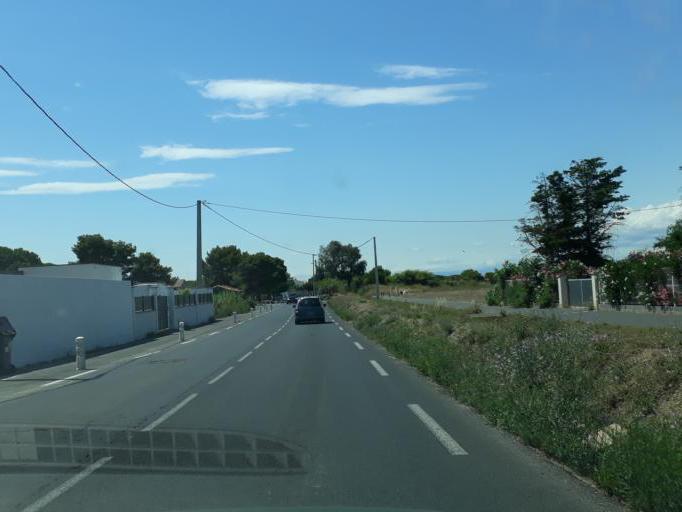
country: FR
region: Languedoc-Roussillon
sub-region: Departement de l'Herault
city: Agde
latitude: 43.2884
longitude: 3.4730
